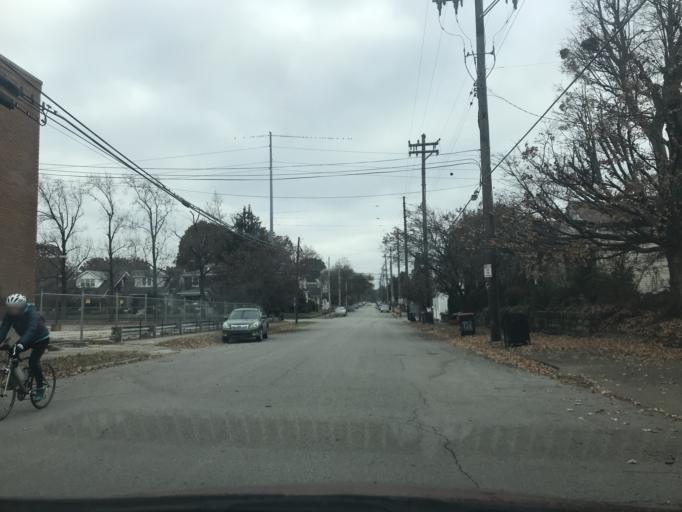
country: US
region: Kentucky
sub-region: Jefferson County
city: Louisville
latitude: 38.2401
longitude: -85.7333
